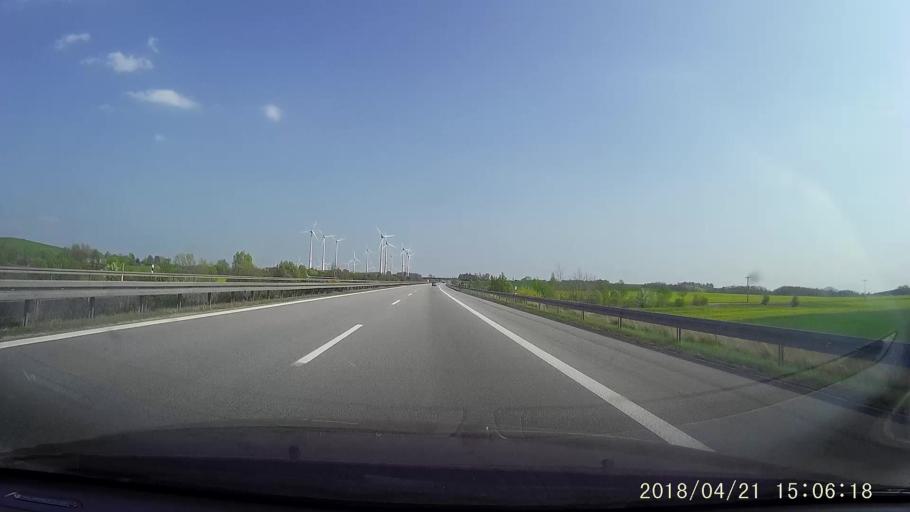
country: DE
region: Saxony
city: Kodersdorf
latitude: 51.2156
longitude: 14.9322
